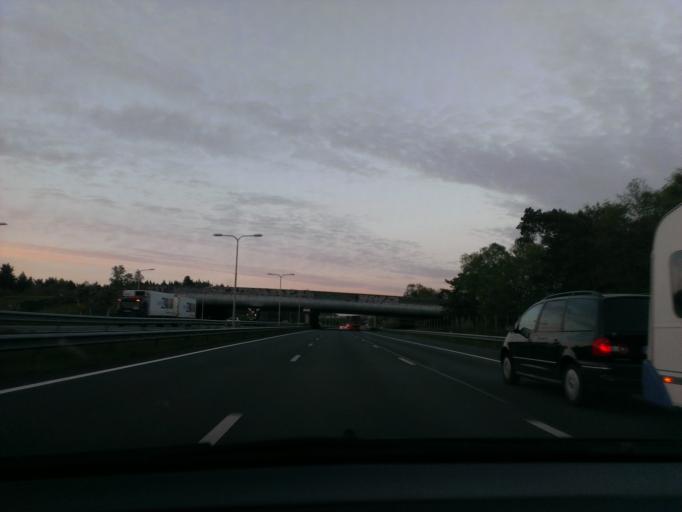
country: NL
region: Gelderland
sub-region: Gemeente Renkum
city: Wolfheze
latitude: 51.9940
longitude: 5.7845
